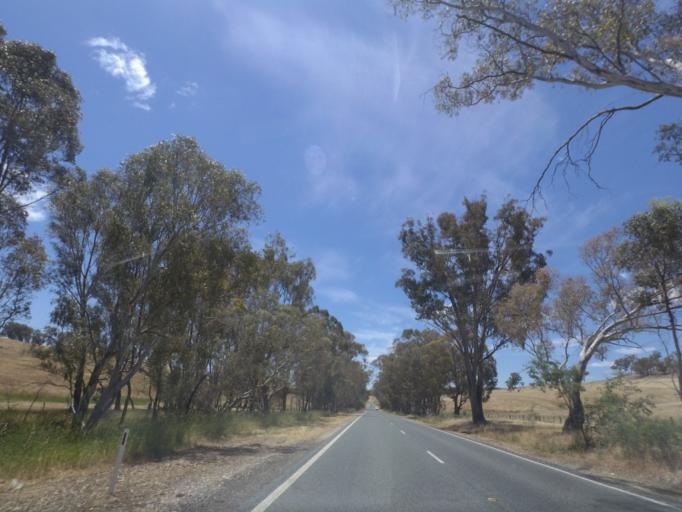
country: AU
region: Victoria
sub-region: Mount Alexander
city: Castlemaine
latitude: -37.1966
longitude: 144.1471
